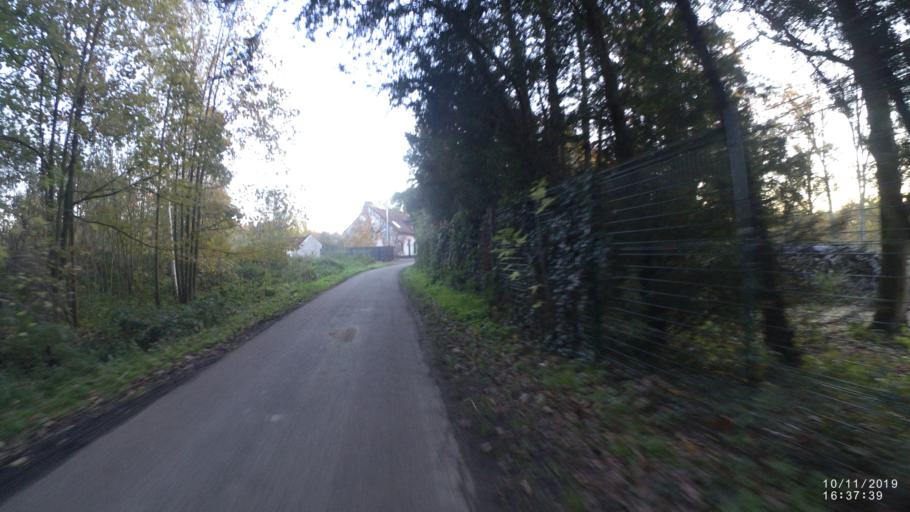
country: BE
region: Flanders
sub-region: Provincie Vlaams-Brabant
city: Bierbeek
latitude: 50.8669
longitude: 4.7754
